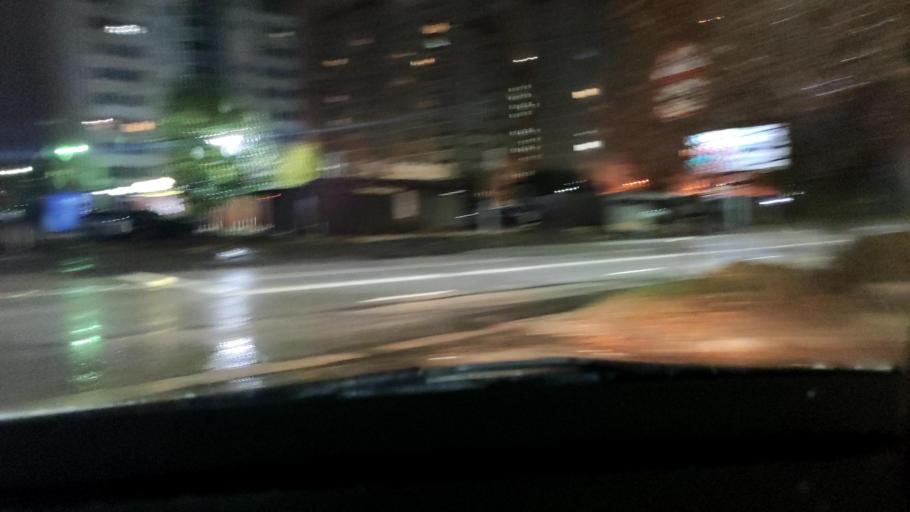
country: RU
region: Voronezj
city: Podgornoye
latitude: 51.7138
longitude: 39.1622
